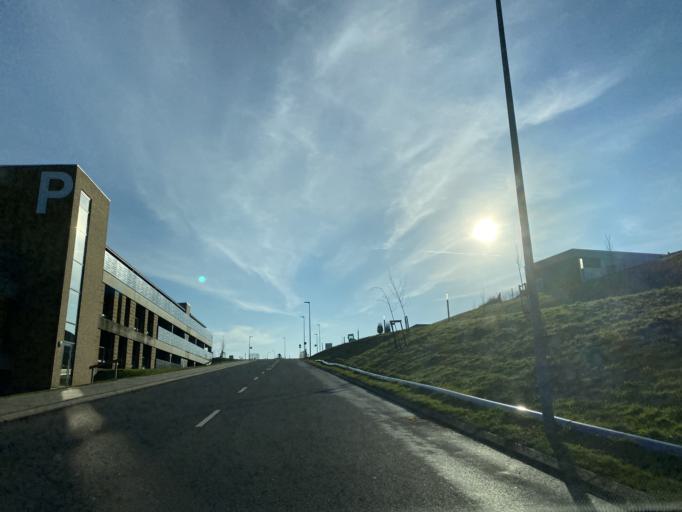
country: DK
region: South Denmark
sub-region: Aabenraa Kommune
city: Aabenraa
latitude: 55.0656
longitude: 9.3775
